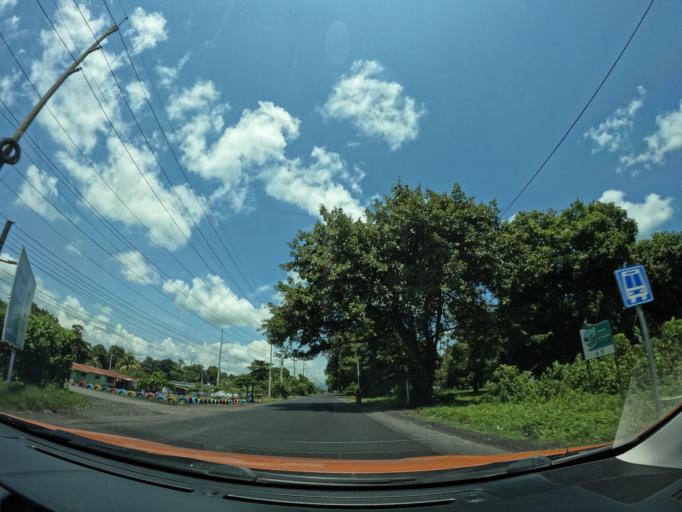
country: GT
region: Escuintla
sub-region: Municipio de Masagua
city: Masagua
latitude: 14.2224
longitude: -90.8302
